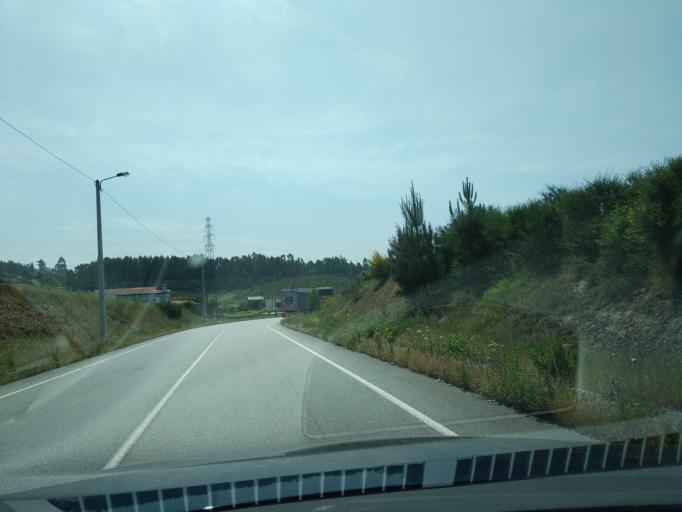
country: PT
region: Porto
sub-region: Paredes
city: Gandra
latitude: 41.2064
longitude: -8.4439
